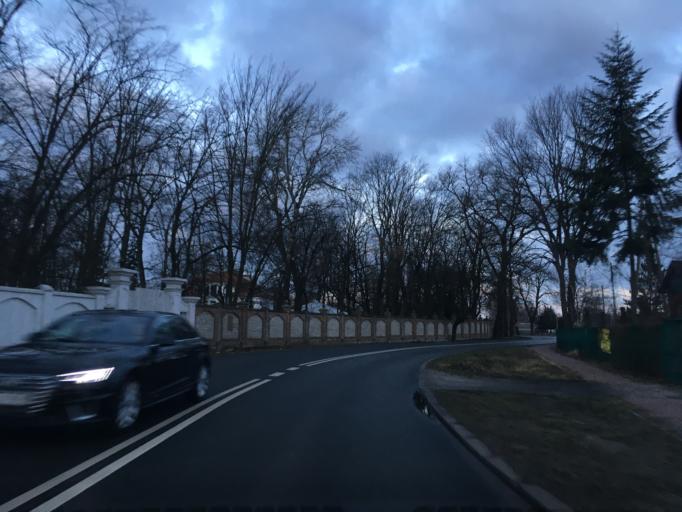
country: PL
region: Masovian Voivodeship
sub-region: Powiat grodziski
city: Milanowek
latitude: 52.0890
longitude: 20.6745
